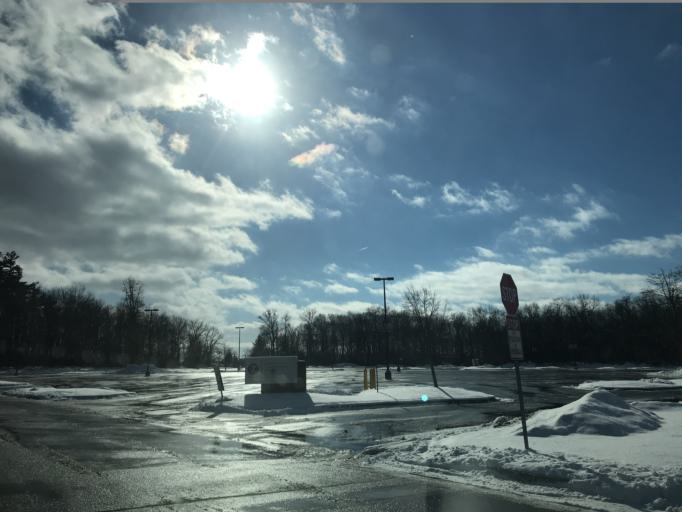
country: US
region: Michigan
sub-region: Washtenaw County
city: Ypsilanti
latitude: 42.2624
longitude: -83.6674
